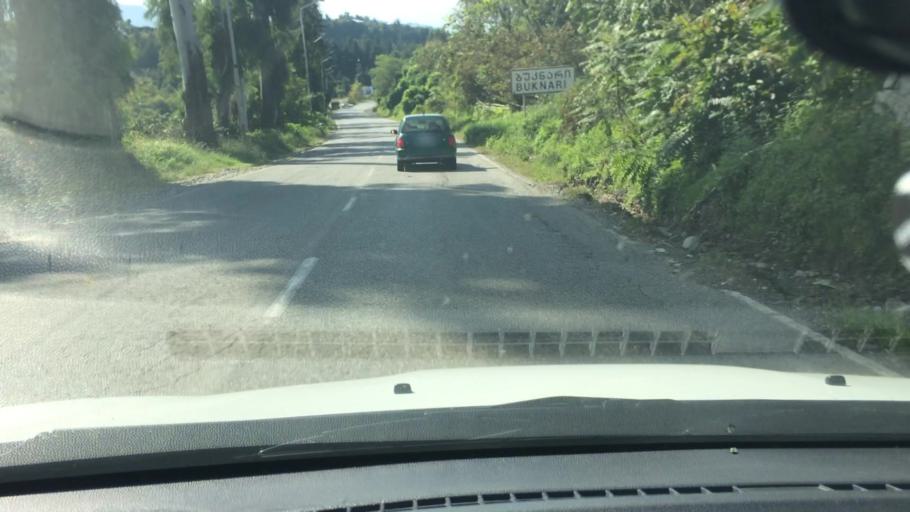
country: GE
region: Ajaria
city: Kobuleti
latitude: 41.7489
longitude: 41.7420
